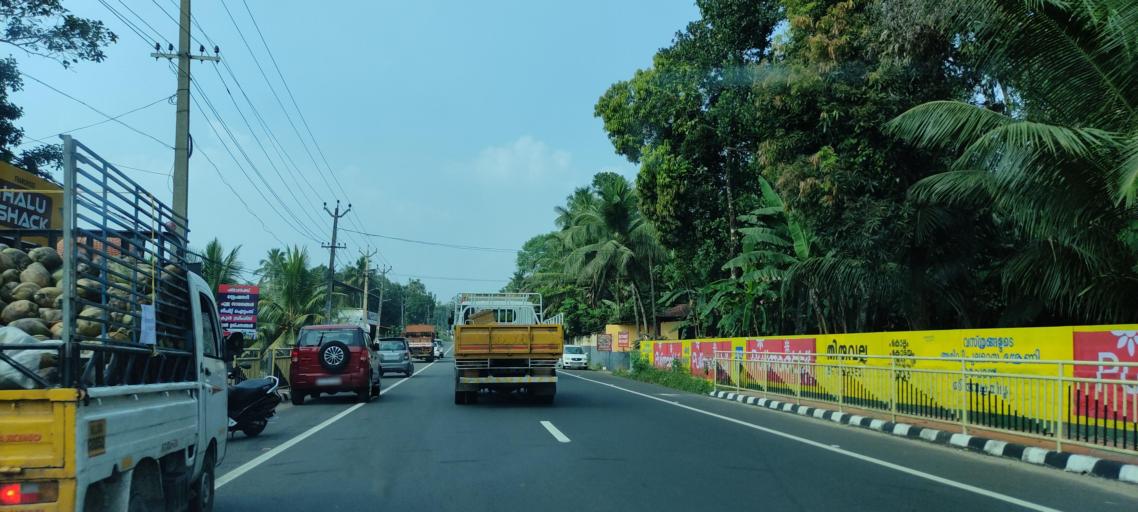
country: IN
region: Kerala
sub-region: Alappuzha
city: Chengannur
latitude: 9.2622
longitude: 76.6569
